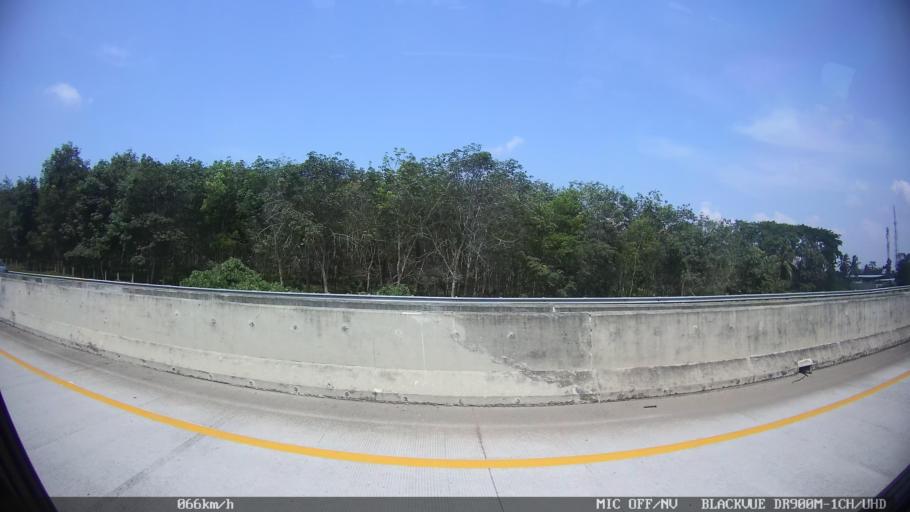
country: ID
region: Lampung
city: Kedaton
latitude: -5.3548
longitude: 105.3237
